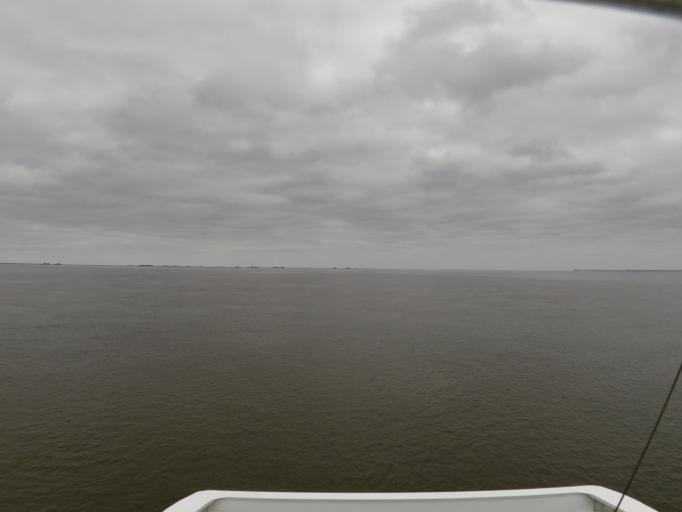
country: DE
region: Schleswig-Holstein
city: Wyk auf Fohr
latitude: 54.6865
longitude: 8.6171
